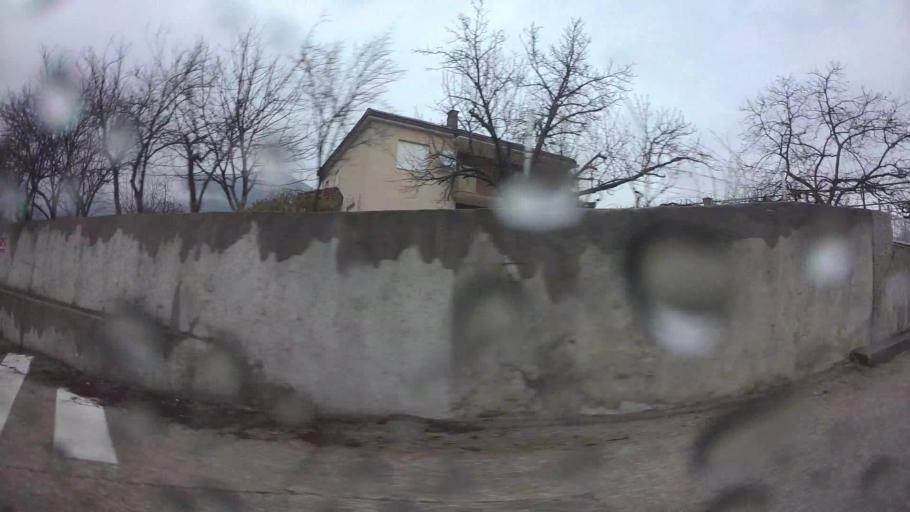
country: BA
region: Federation of Bosnia and Herzegovina
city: Cim
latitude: 43.3474
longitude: 17.7818
